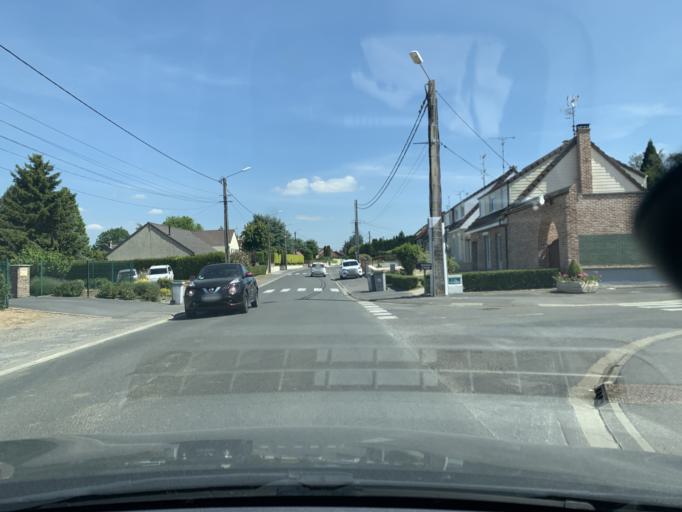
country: FR
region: Nord-Pas-de-Calais
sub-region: Departement du Nord
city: Fontaine-au-Pire
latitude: 50.1309
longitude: 3.3833
